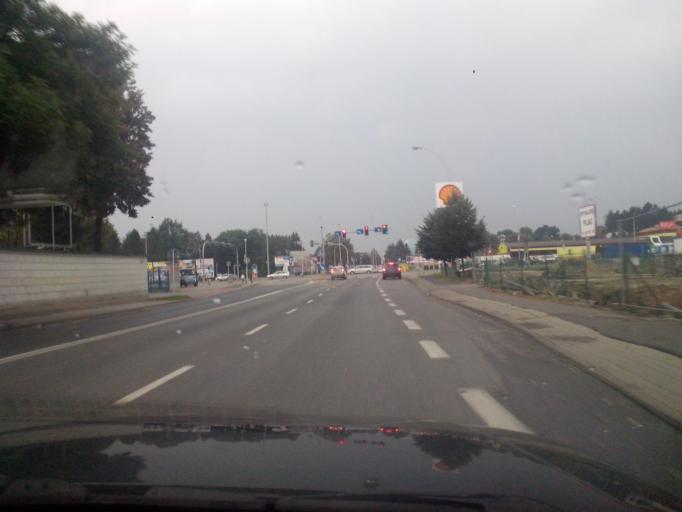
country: PL
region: Subcarpathian Voivodeship
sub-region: Rzeszow
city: Rzeszow
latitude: 50.0211
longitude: 21.9947
